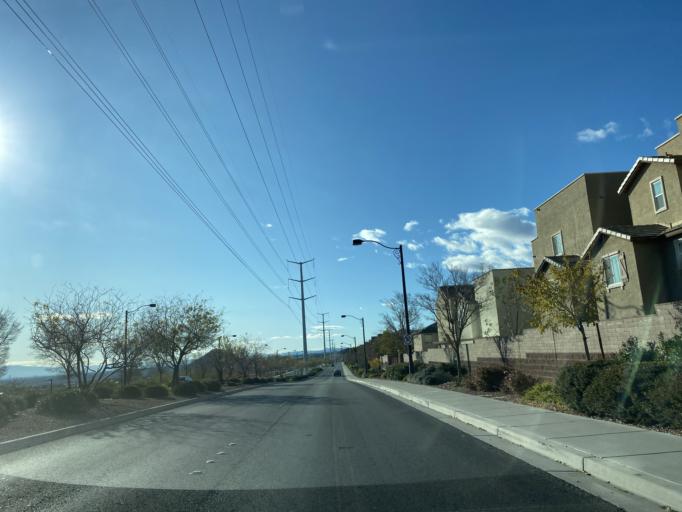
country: US
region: Nevada
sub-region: Clark County
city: Summerlin South
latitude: 36.2871
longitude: -115.3290
